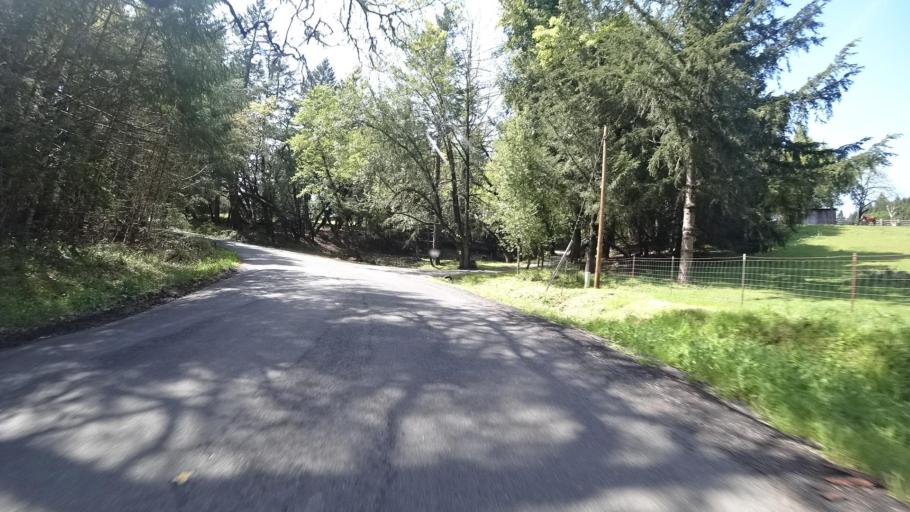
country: US
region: California
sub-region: Humboldt County
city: Redway
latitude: 40.3901
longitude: -123.7438
